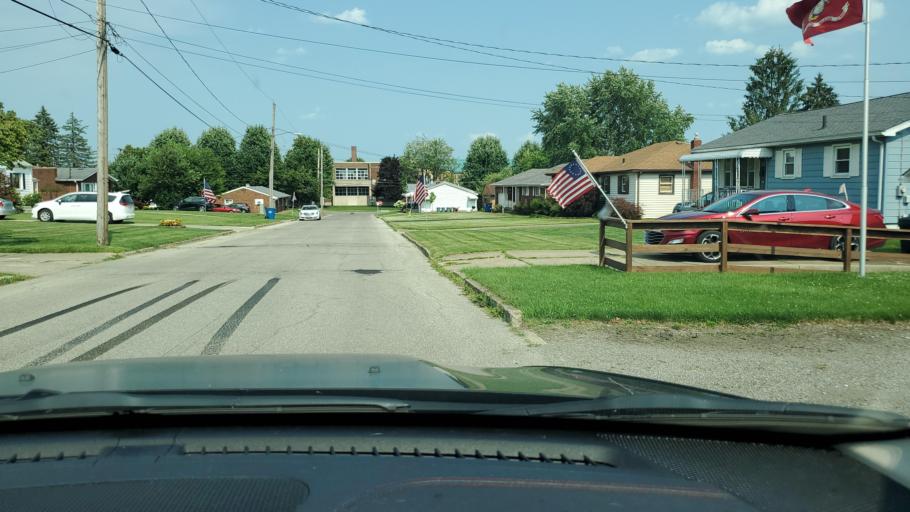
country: US
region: Ohio
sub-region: Mahoning County
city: Struthers
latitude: 41.0490
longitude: -80.6052
